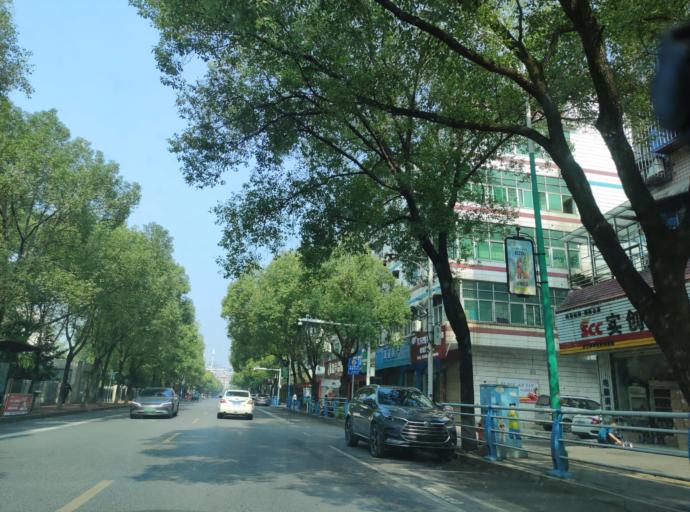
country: CN
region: Jiangxi Sheng
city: Pingxiang
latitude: 27.6424
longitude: 113.8558
